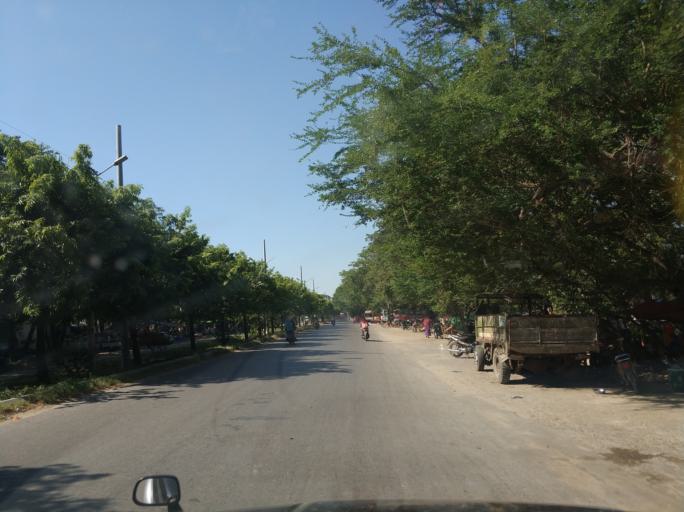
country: MM
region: Mandalay
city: Mandalay
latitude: 21.9662
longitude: 96.0561
